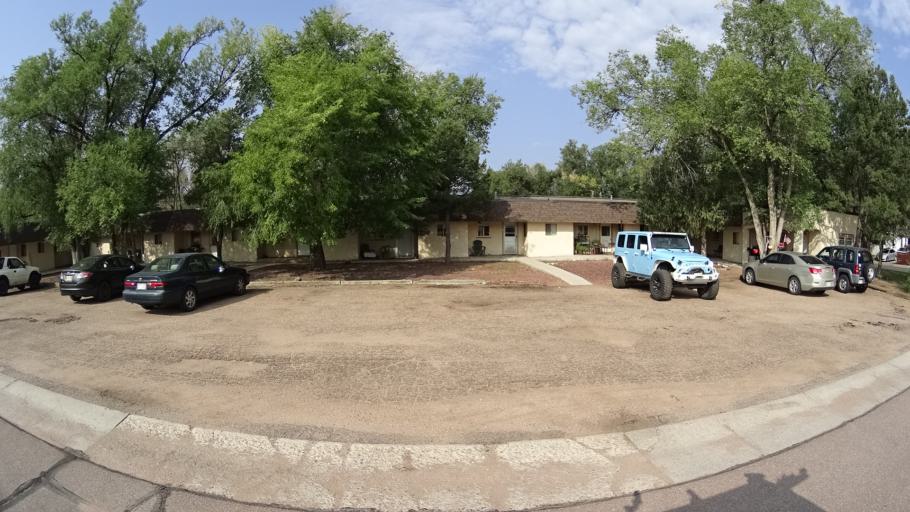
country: US
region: Colorado
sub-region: El Paso County
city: Colorado Springs
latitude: 38.8418
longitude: -104.7827
